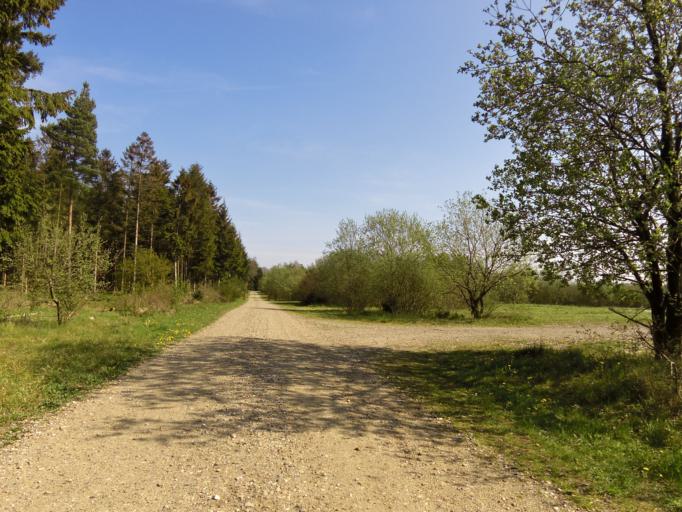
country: DK
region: South Denmark
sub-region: Tonder Kommune
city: Logumkloster
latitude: 55.1812
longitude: 8.9369
